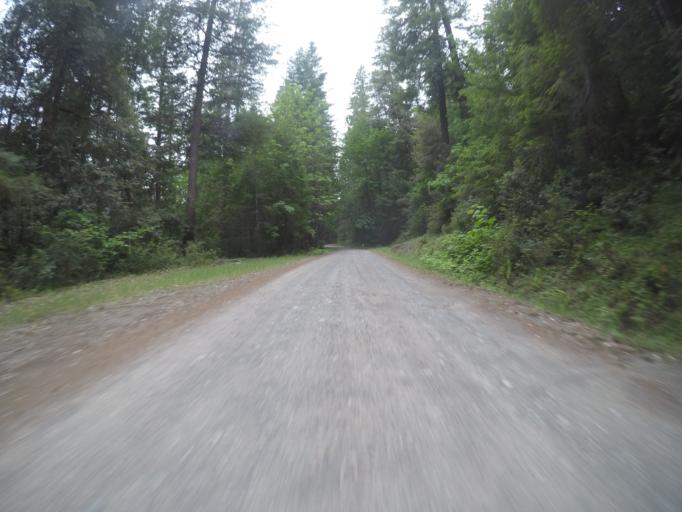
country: US
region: California
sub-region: Del Norte County
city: Bertsch-Oceanview
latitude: 41.7255
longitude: -123.8942
